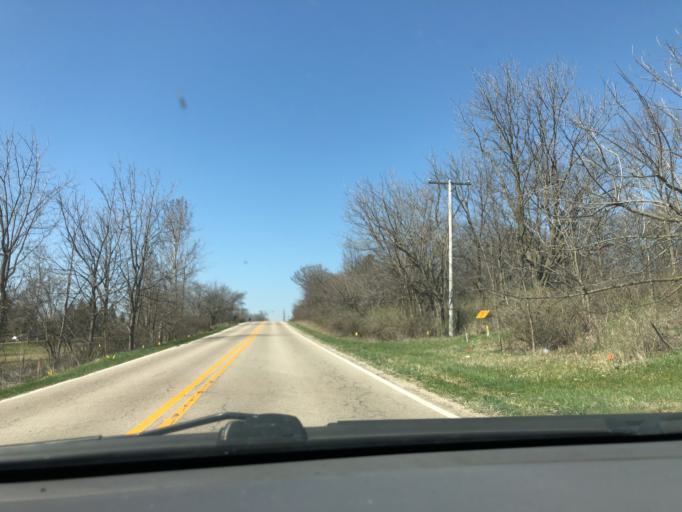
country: US
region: Illinois
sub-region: Kane County
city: Hampshire
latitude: 42.1096
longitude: -88.4912
